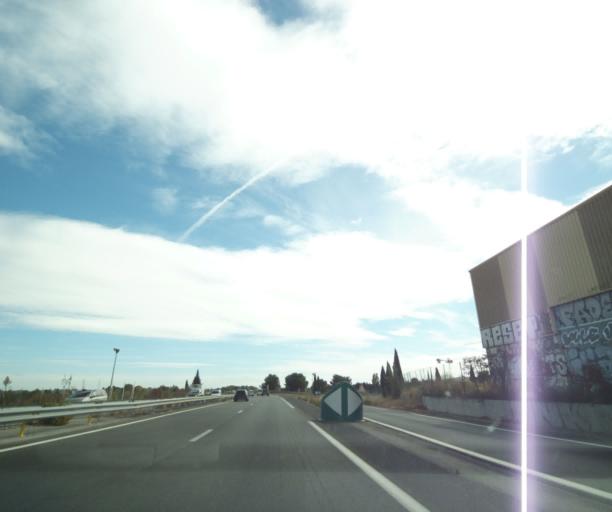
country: FR
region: Languedoc-Roussillon
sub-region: Departement de l'Herault
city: Juvignac
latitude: 43.6202
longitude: 3.7912
